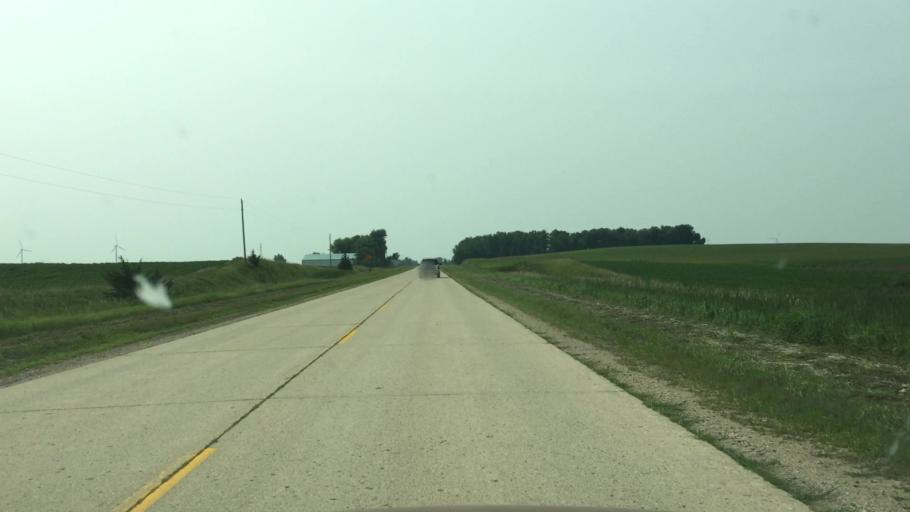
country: US
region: Iowa
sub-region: Dickinson County
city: Lake Park
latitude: 43.4246
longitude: -95.2891
